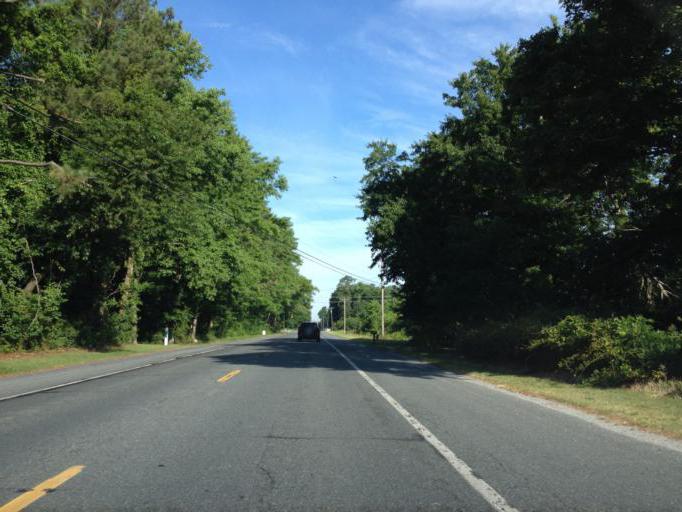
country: US
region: Delaware
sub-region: Sussex County
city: Millsboro
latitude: 38.5605
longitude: -75.2656
